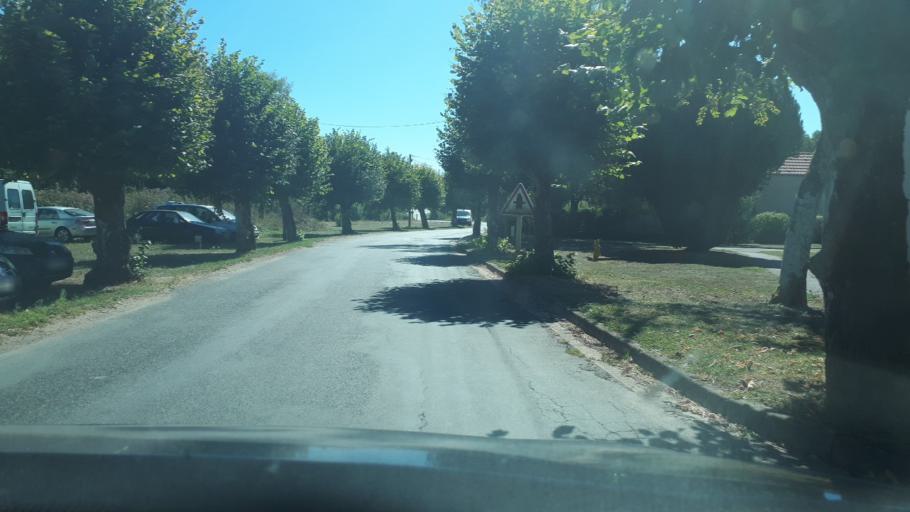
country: FR
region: Centre
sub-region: Departement du Cher
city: Sancerre
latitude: 47.2531
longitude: 2.7601
